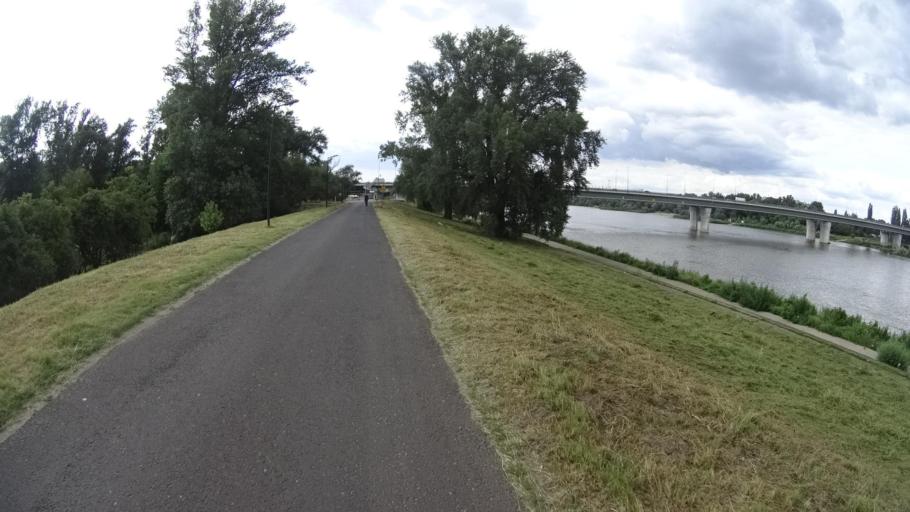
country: PL
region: Masovian Voivodeship
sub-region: Warszawa
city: Mokotow
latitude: 52.2231
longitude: 21.0494
